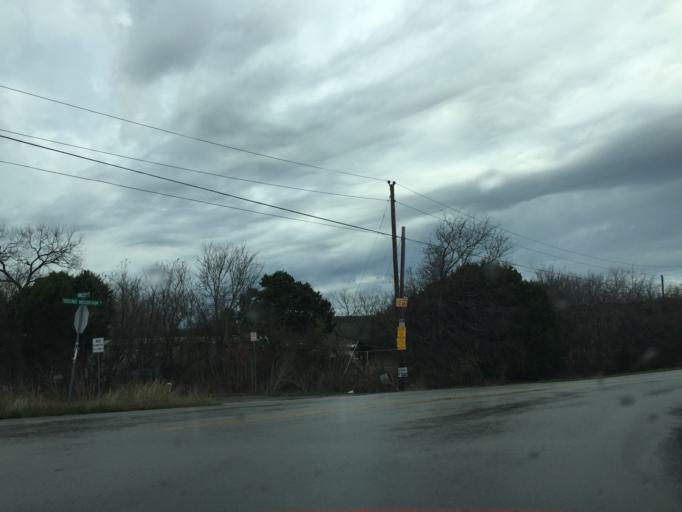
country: US
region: Texas
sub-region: Travis County
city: Jonestown
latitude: 30.5691
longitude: -97.9442
